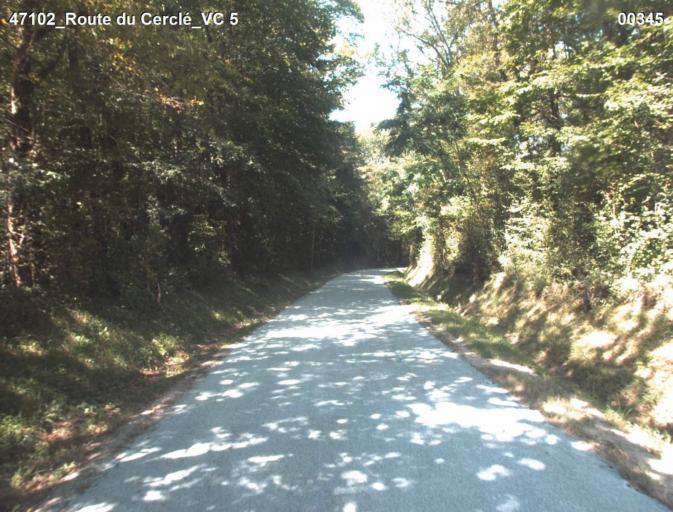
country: FR
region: Aquitaine
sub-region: Departement du Lot-et-Garonne
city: Laplume
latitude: 44.0723
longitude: 0.4575
